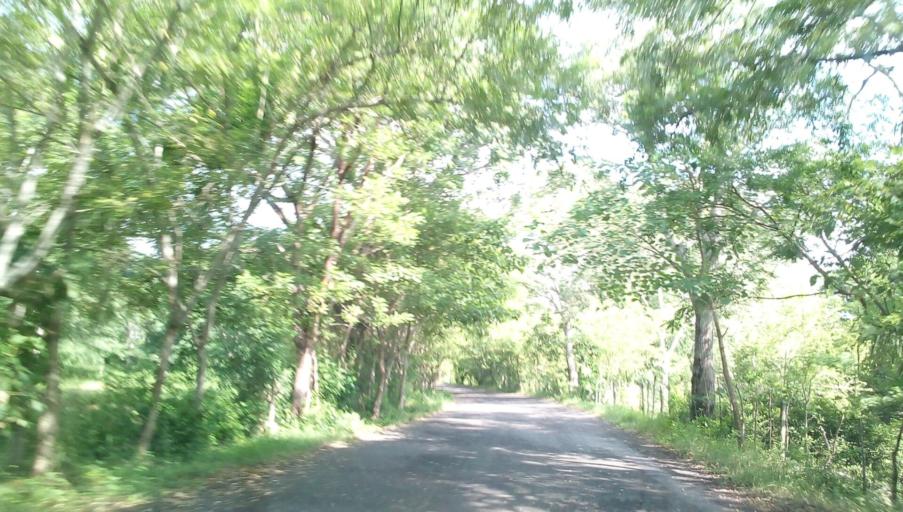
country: MX
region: Veracruz
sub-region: Citlaltepetl
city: Las Sabinas
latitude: 21.3537
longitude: -97.8976
